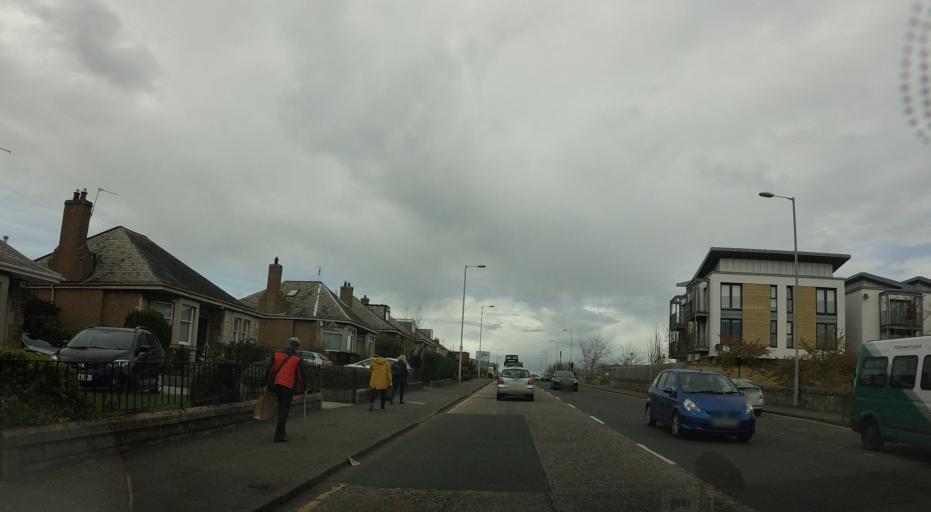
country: GB
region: Scotland
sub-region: Edinburgh
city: Edinburgh
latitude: 55.9665
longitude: -3.2348
